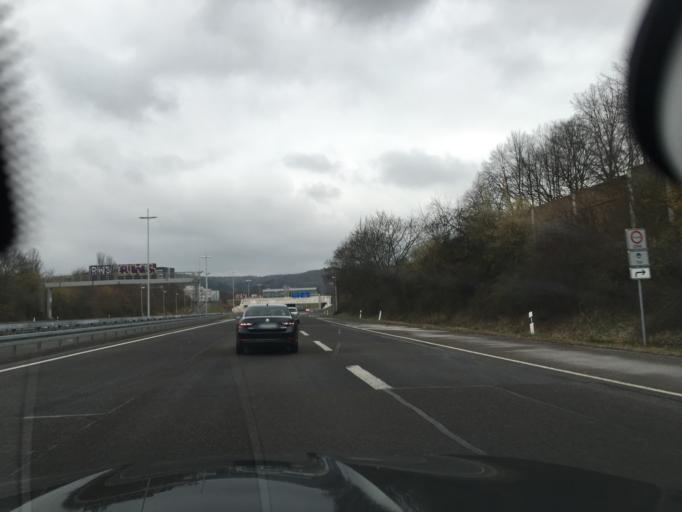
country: DE
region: North Rhine-Westphalia
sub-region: Regierungsbezirk Koln
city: Bonn
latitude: 50.7085
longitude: 7.1357
